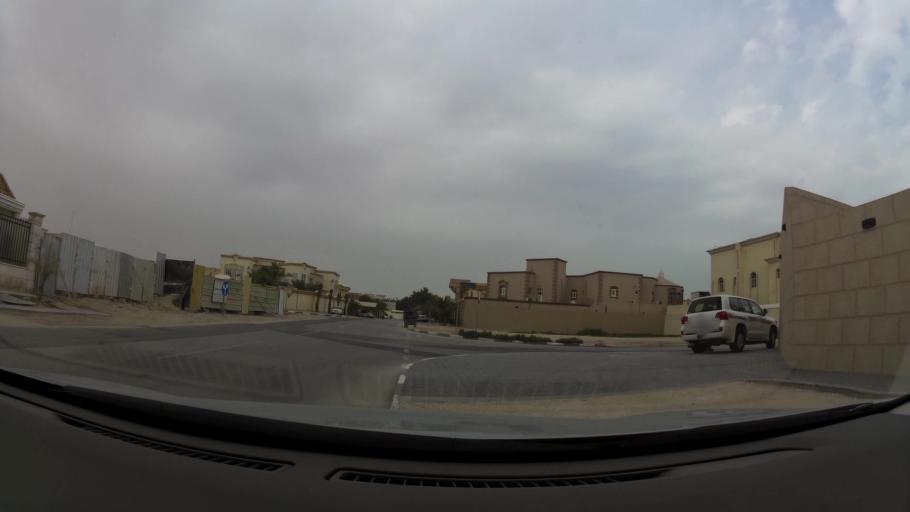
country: QA
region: Baladiyat ar Rayyan
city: Ar Rayyan
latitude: 25.3439
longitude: 51.4753
